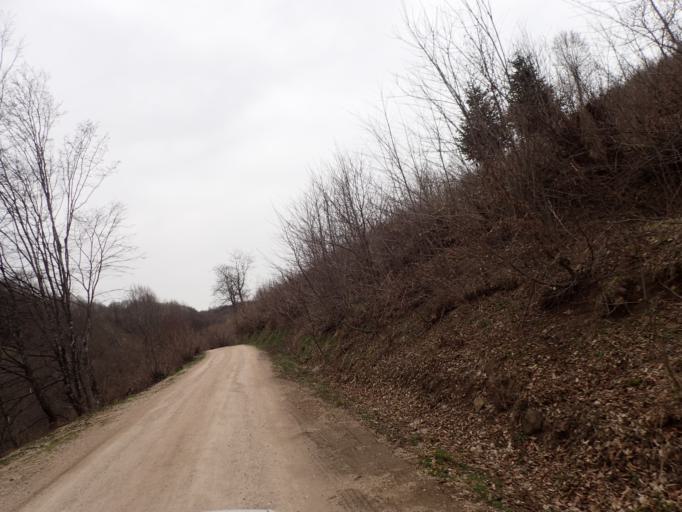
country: TR
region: Ordu
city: Kumru
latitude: 40.8058
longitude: 37.1664
